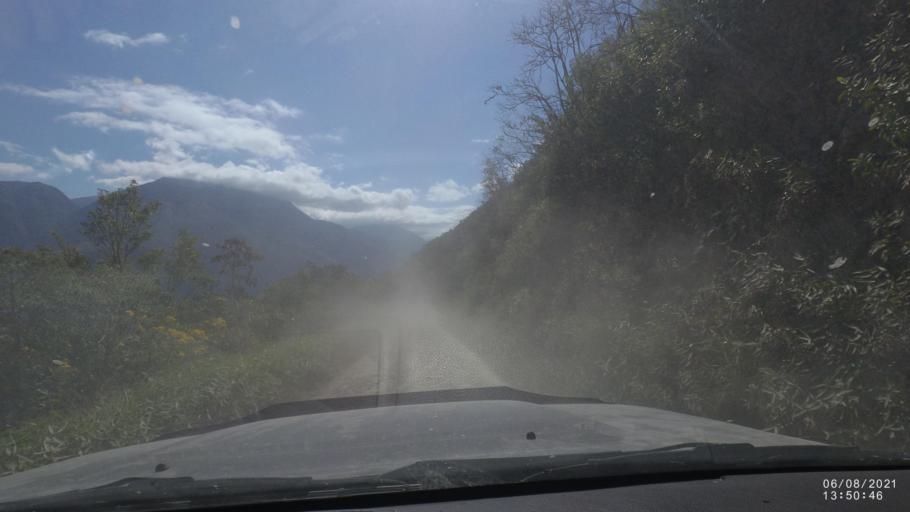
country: BO
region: La Paz
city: Quime
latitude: -16.6554
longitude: -66.7240
